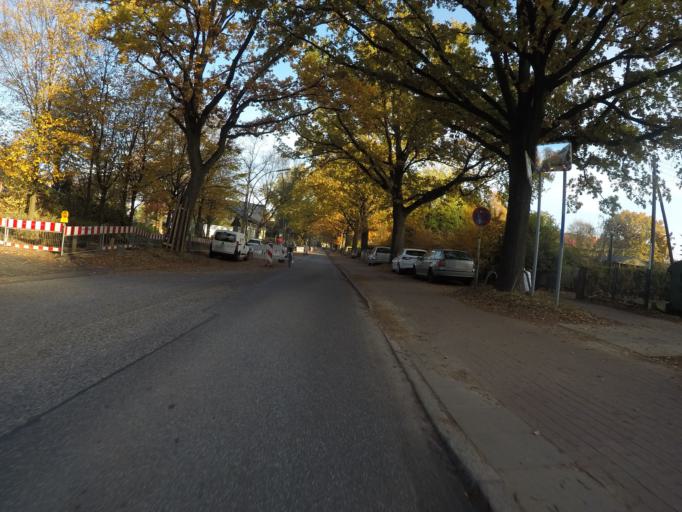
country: DE
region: Hamburg
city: Hamburg-Nord
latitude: 53.5855
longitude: 9.9561
